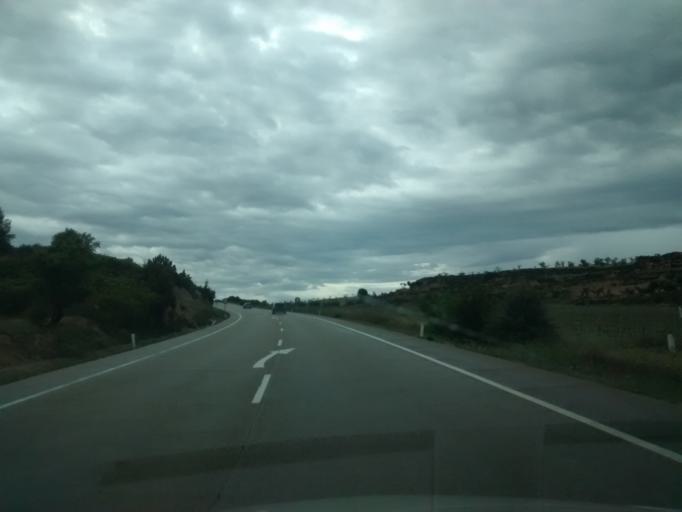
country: ES
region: Aragon
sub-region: Provincia de Zaragoza
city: Maella
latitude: 41.1394
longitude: 0.1208
